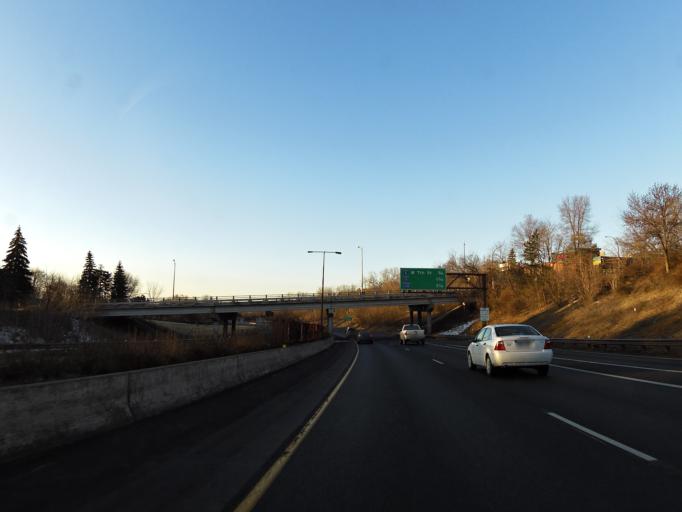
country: US
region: Minnesota
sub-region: Dakota County
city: West Saint Paul
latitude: 44.9278
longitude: -93.1446
